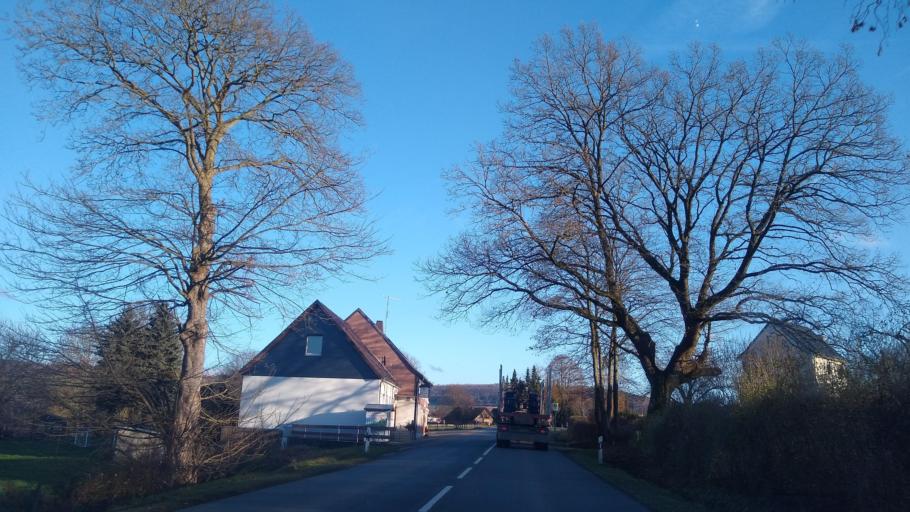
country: DE
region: North Rhine-Westphalia
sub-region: Regierungsbezirk Detmold
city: Hoexter
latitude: 51.8000
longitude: 9.3449
